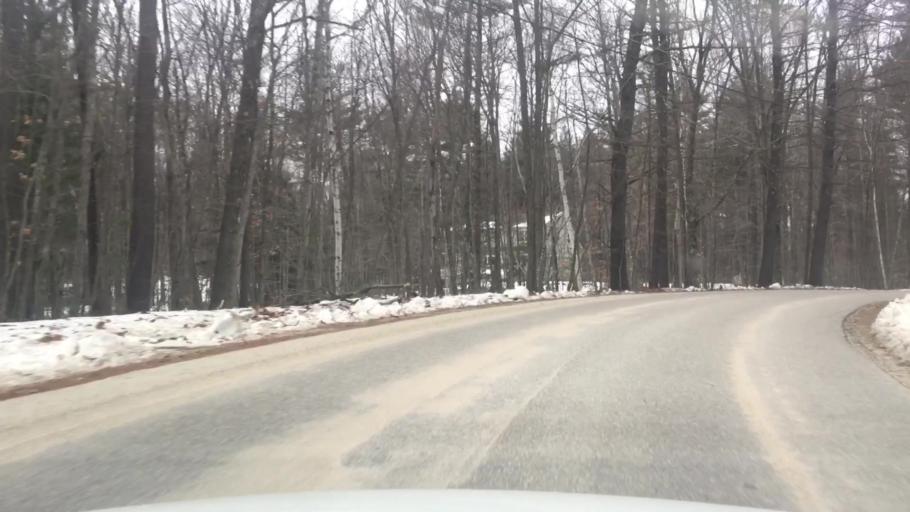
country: US
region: New Hampshire
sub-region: Merrimack County
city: Hopkinton
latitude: 43.1727
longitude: -71.6751
